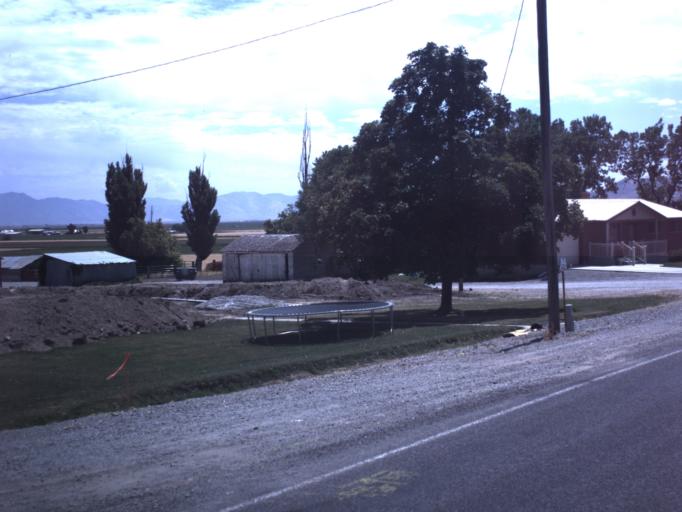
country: US
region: Utah
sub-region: Box Elder County
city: Tremonton
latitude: 41.6877
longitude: -112.2971
